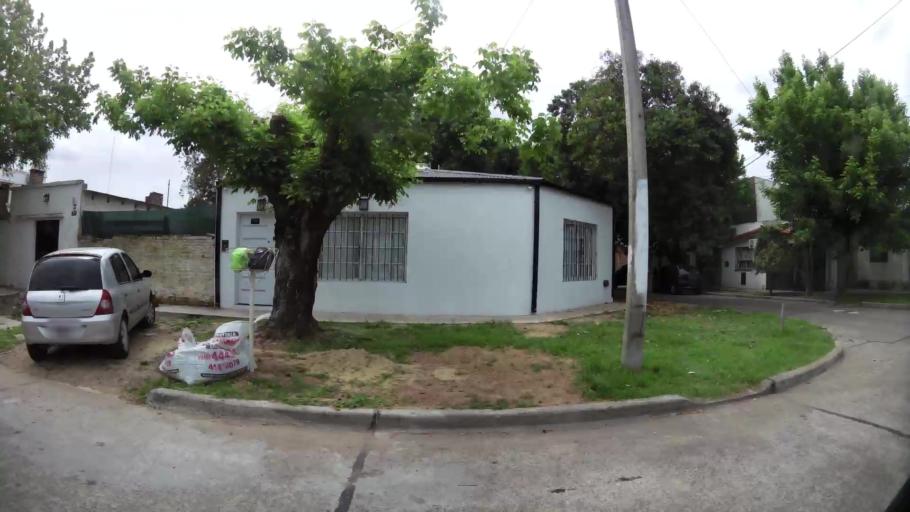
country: AR
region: Buenos Aires
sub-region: Partido de Campana
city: Campana
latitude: -34.1680
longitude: -58.9728
